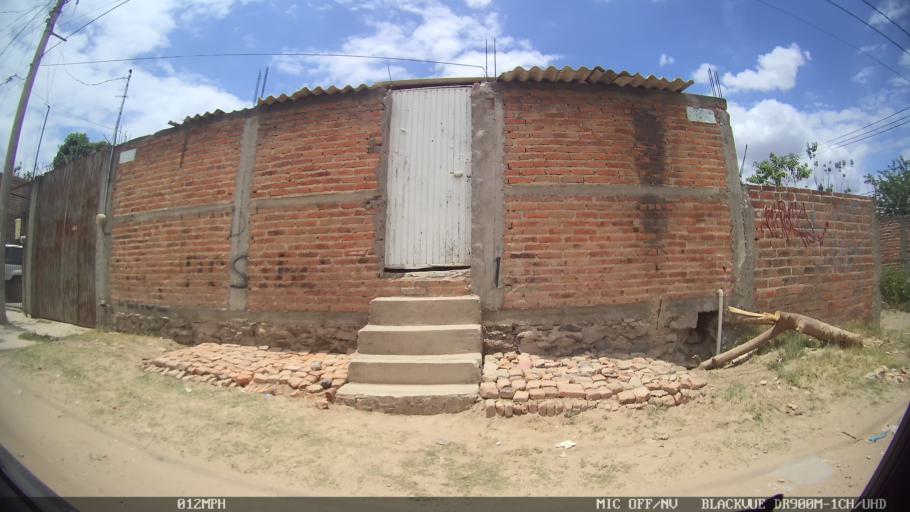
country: MX
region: Jalisco
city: Tlaquepaque
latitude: 20.6409
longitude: -103.2669
